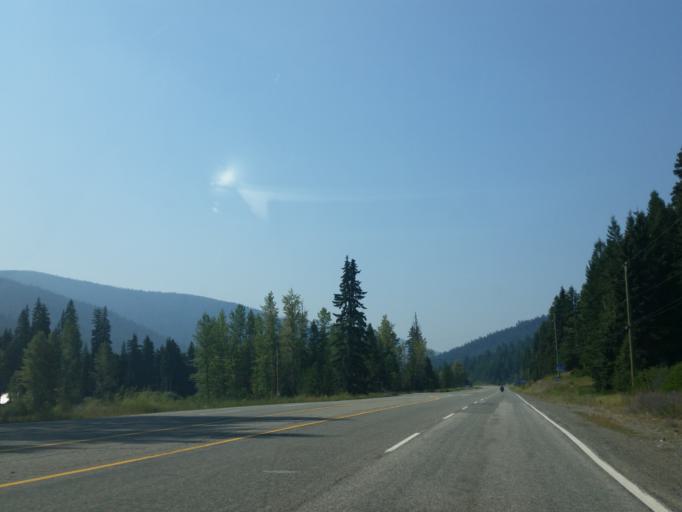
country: CA
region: British Columbia
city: Princeton
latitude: 49.1409
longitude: -120.6122
